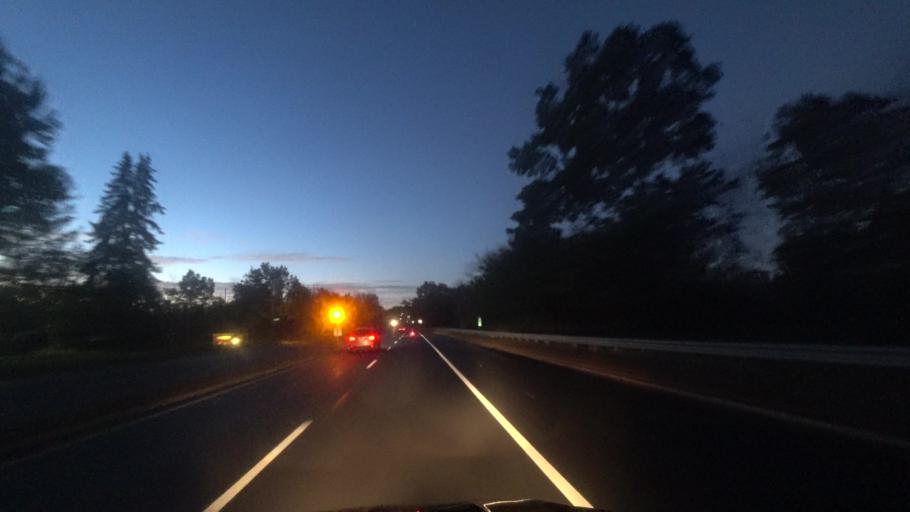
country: US
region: Massachusetts
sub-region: Middlesex County
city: North Reading
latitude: 42.6024
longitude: -71.1219
